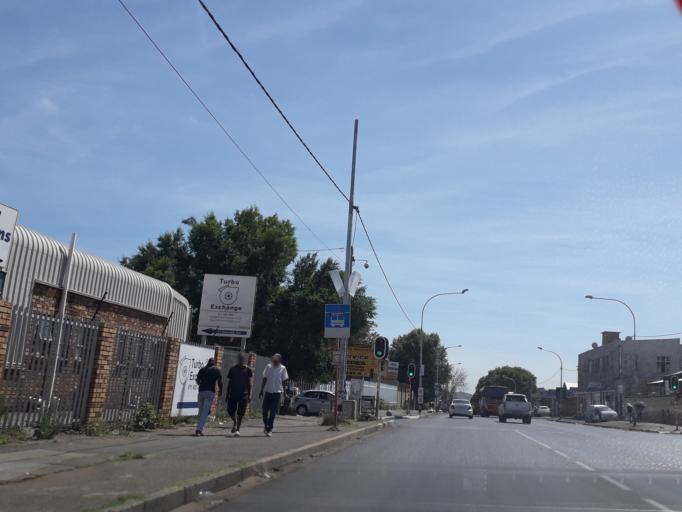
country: ZA
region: Gauteng
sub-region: City of Johannesburg Metropolitan Municipality
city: Johannesburg
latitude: -26.2014
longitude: 28.0632
